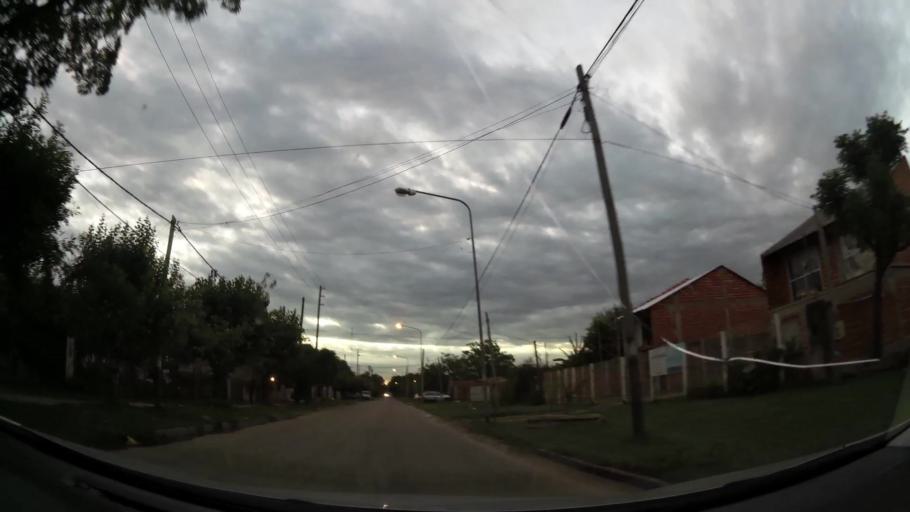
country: AR
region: Buenos Aires
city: Santa Catalina - Dique Lujan
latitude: -34.4165
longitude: -58.6816
